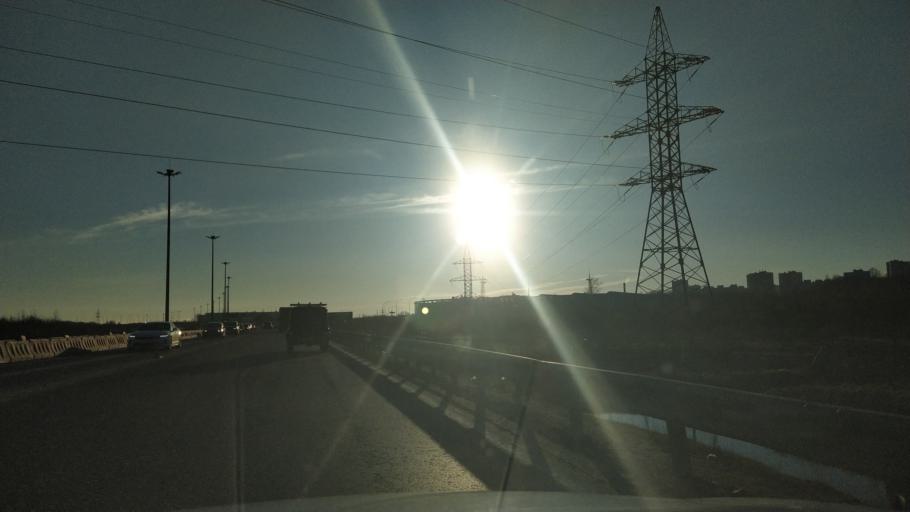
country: RU
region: St.-Petersburg
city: Pargolovo
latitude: 60.0995
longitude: 30.2832
